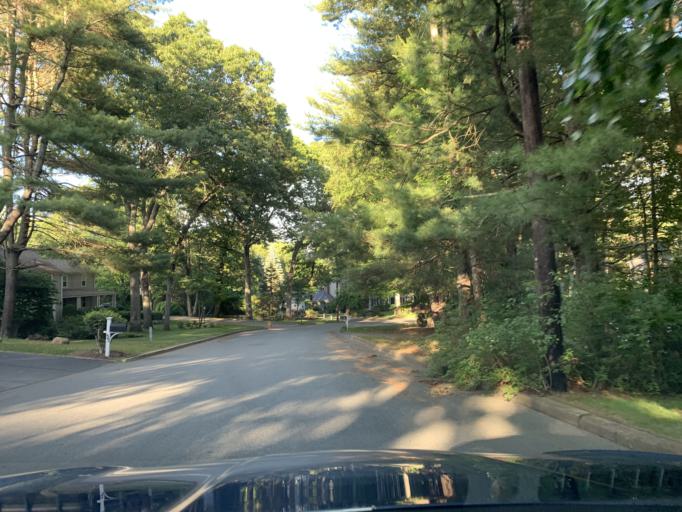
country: US
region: Rhode Island
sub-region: Kent County
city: East Greenwich
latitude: 41.6457
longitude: -71.4831
